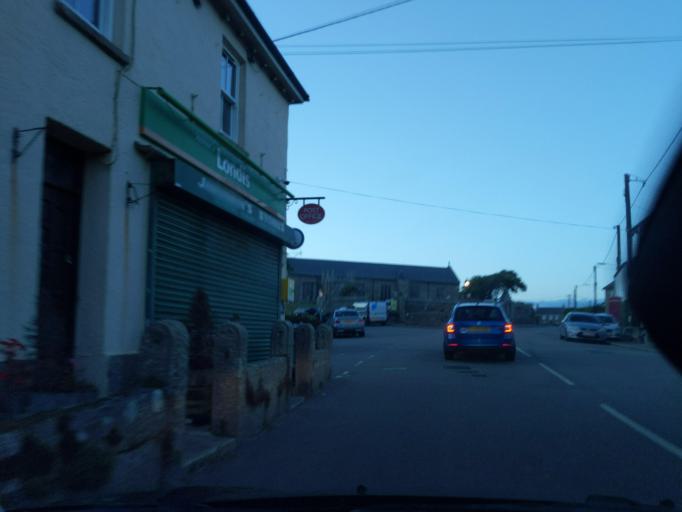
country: GB
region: England
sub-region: Cornwall
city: St. Buryan
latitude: 50.0742
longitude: -5.6230
